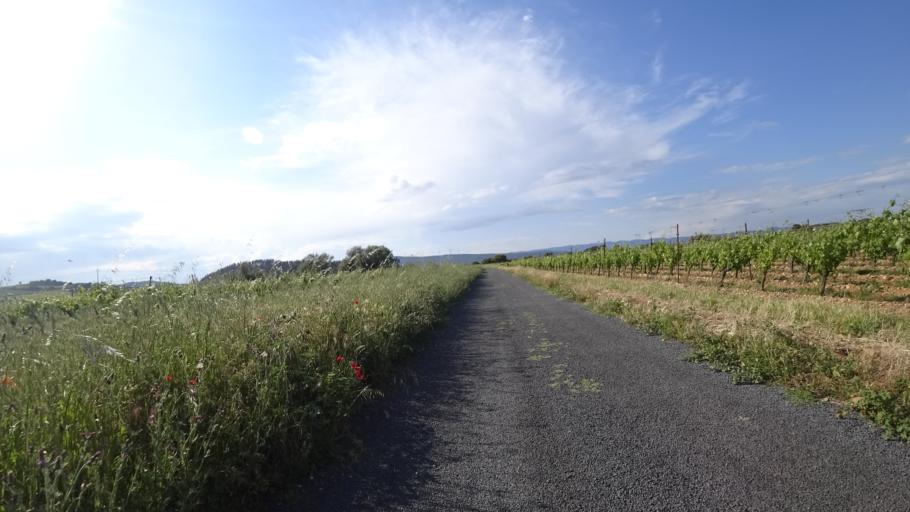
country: FR
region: Languedoc-Roussillon
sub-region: Departement de l'Aude
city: Canet
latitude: 43.2593
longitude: 2.8300
